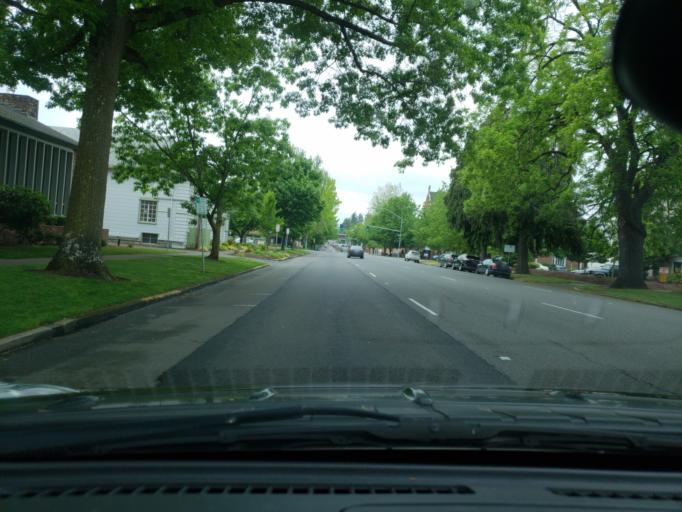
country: US
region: Oregon
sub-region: Marion County
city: Salem
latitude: 44.9428
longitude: -123.0305
